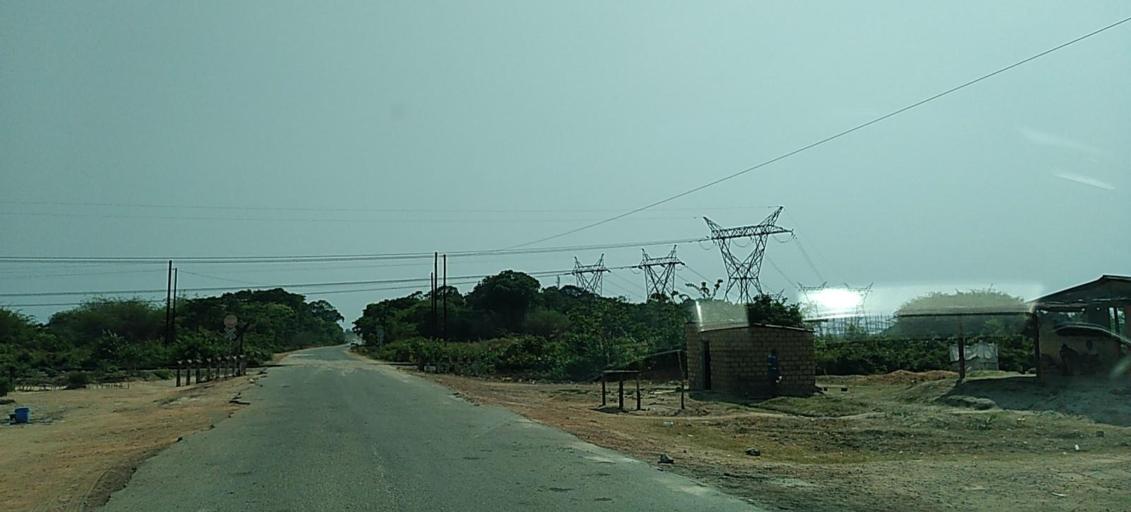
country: ZM
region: Copperbelt
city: Chambishi
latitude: -12.6058
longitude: 27.9733
